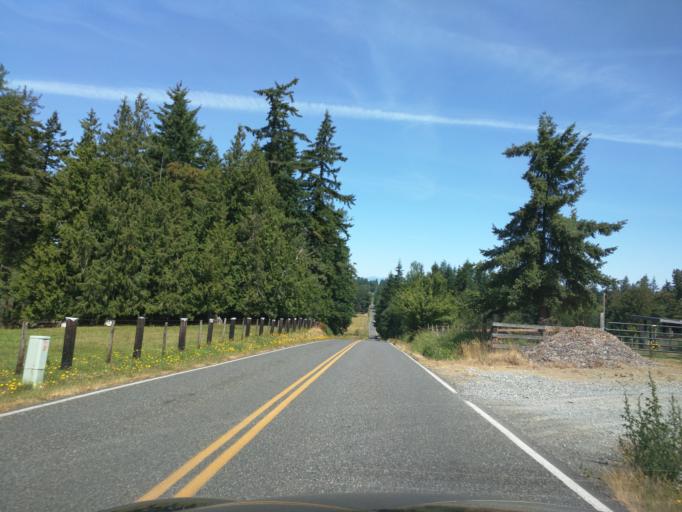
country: US
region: Washington
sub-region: Whatcom County
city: Geneva
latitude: 48.8049
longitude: -122.3989
